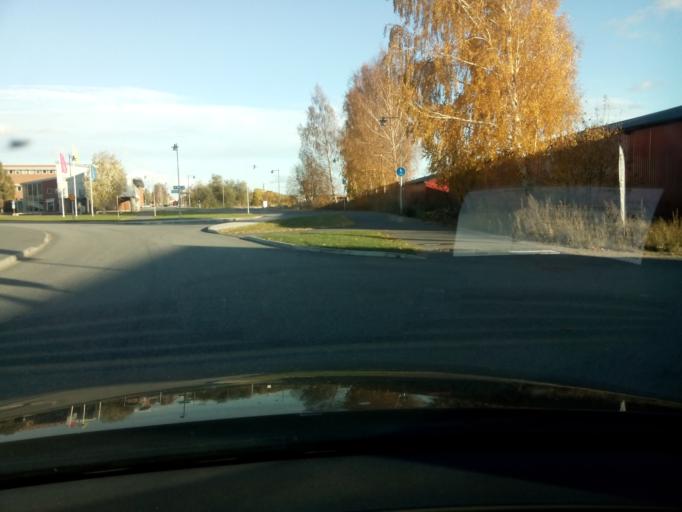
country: SE
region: Soedermanland
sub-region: Nykopings Kommun
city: Nykoping
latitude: 58.7441
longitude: 17.0096
